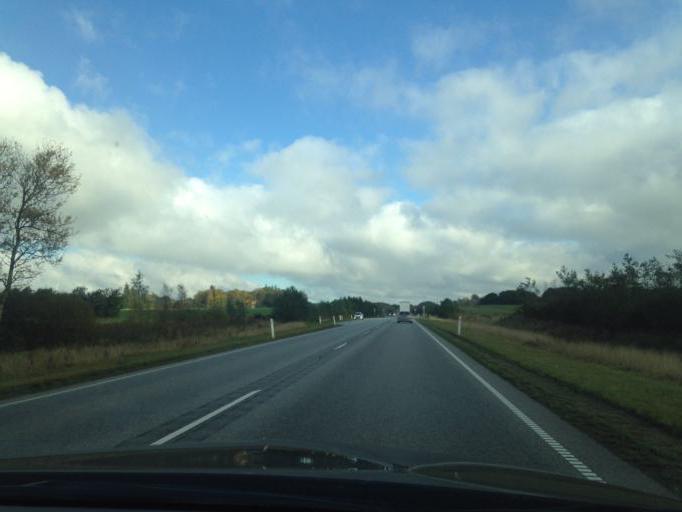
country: DK
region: South Denmark
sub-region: Vejle Kommune
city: Give
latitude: 55.8134
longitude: 9.2343
